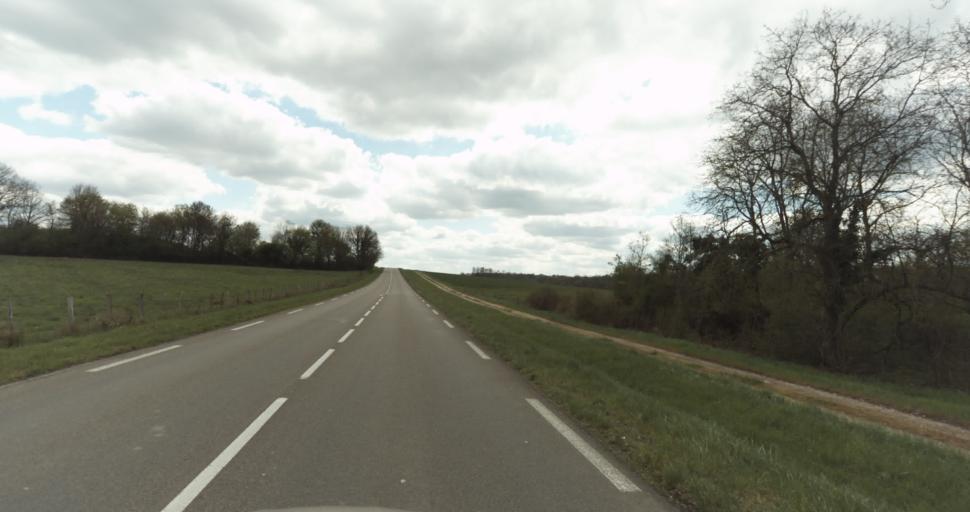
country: FR
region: Bourgogne
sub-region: Departement de la Cote-d'Or
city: Auxonne
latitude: 47.1567
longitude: 5.4137
